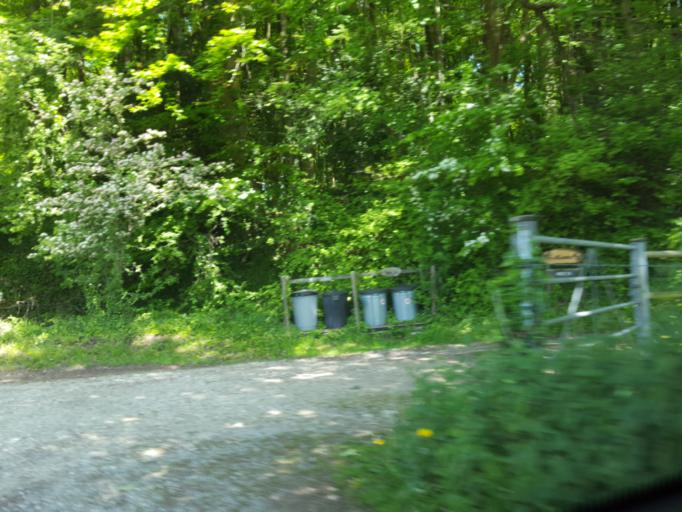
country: GB
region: England
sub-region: Gloucestershire
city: Brimscombe
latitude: 51.7242
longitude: -2.1859
